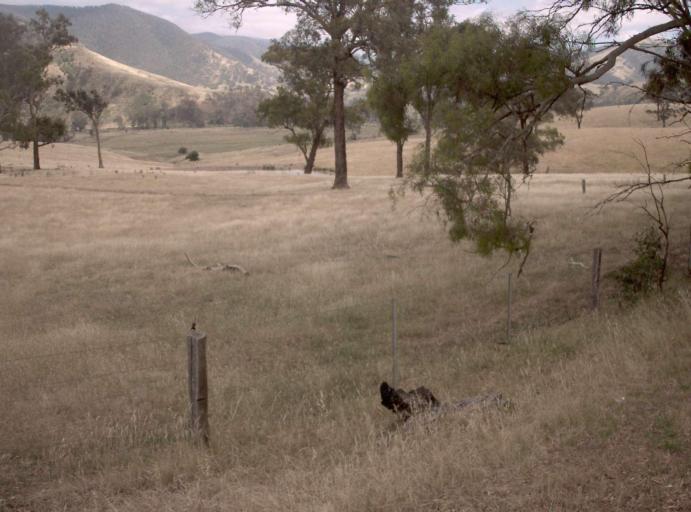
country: AU
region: Victoria
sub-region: Wellington
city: Heyfield
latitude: -37.6559
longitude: 146.6424
